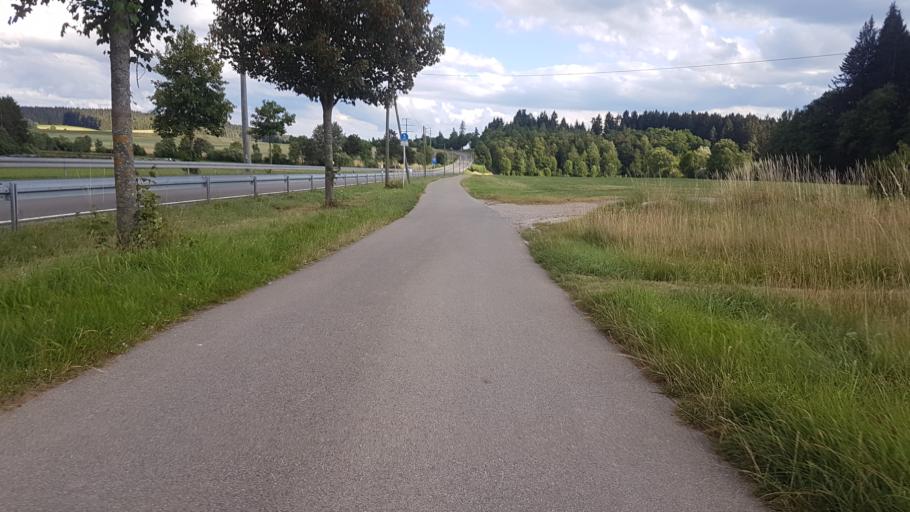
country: DE
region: Baden-Wuerttemberg
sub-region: Freiburg Region
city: Unterkirnach
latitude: 48.0123
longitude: 8.4081
